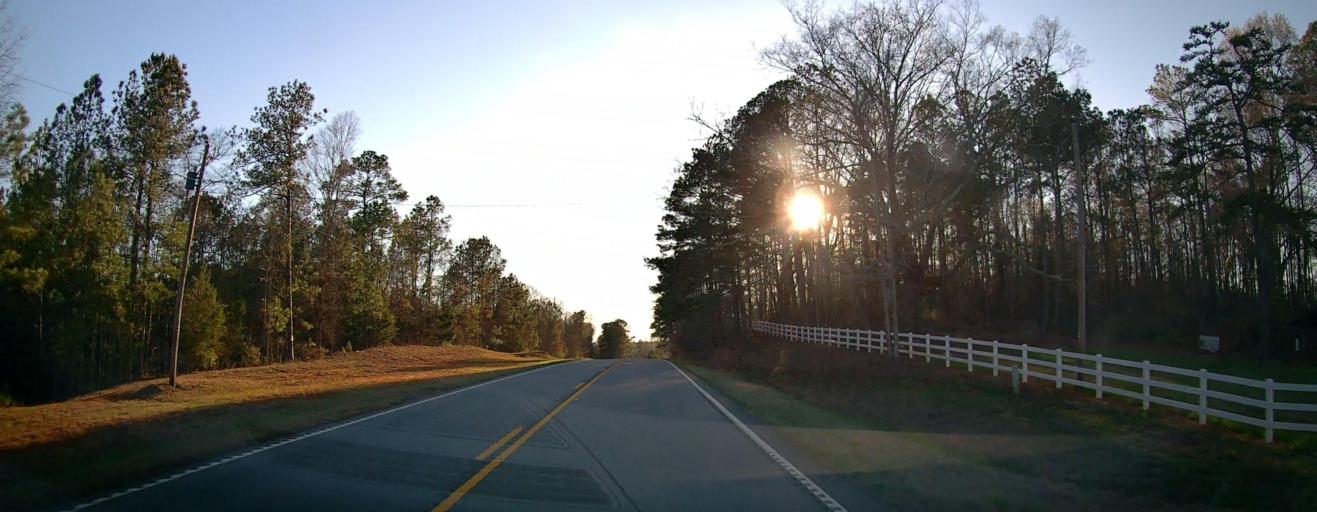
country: US
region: Georgia
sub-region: Talbot County
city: Sardis
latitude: 32.6436
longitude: -84.7052
